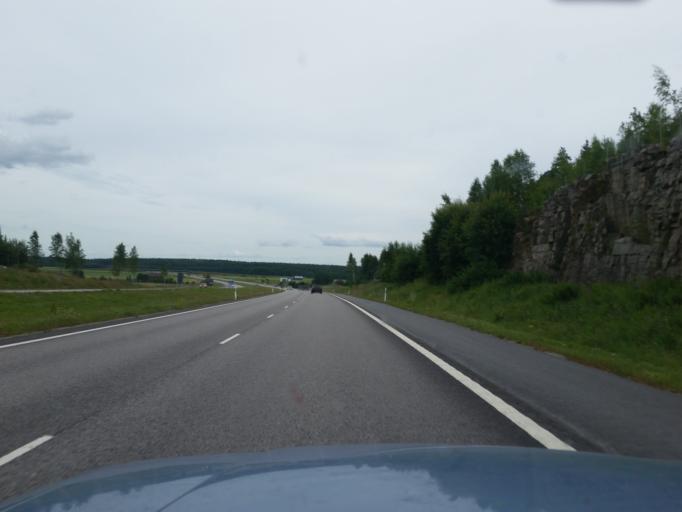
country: FI
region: Varsinais-Suomi
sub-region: Salo
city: Halikko
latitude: 60.4197
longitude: 23.0866
